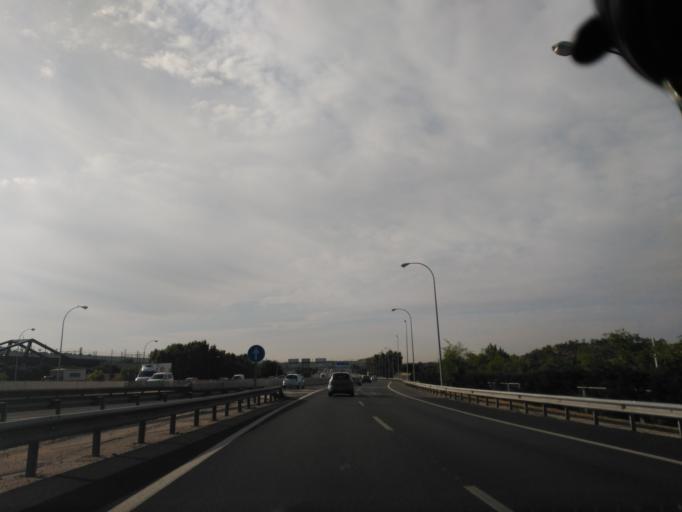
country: ES
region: Madrid
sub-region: Provincia de Madrid
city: Usera
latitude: 40.3791
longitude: -3.6860
